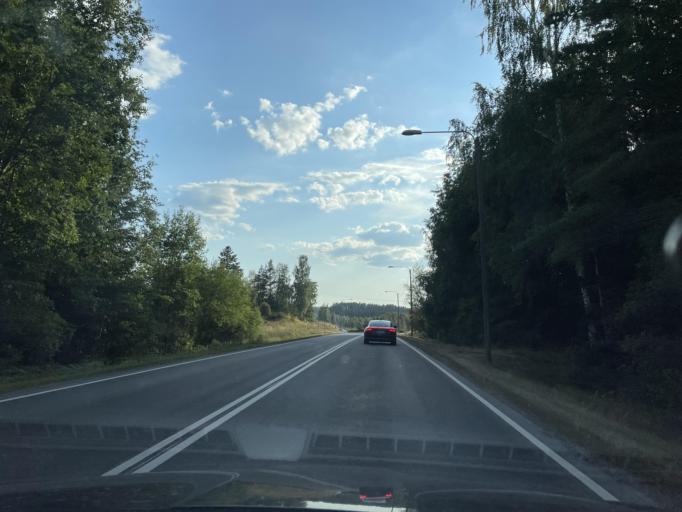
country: FI
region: Haeme
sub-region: Haemeenlinna
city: Tuulos
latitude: 61.1080
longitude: 24.8683
